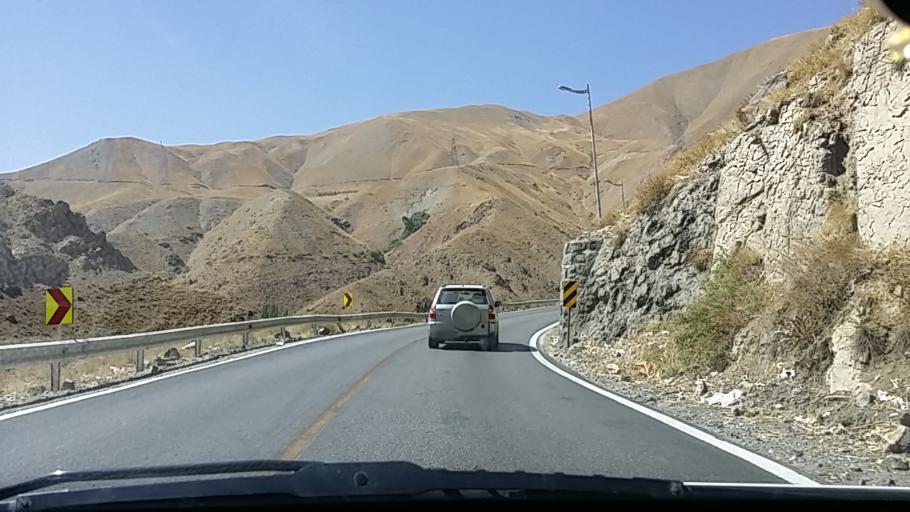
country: IR
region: Tehran
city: Tajrish
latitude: 36.1152
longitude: 51.3246
